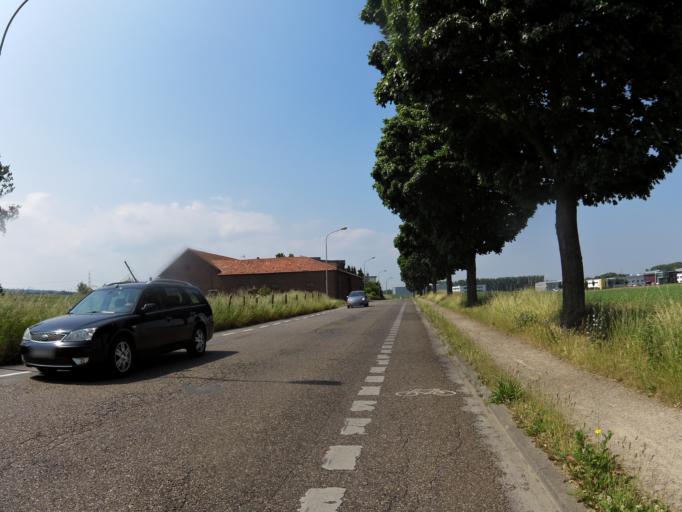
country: DE
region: North Rhine-Westphalia
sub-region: Regierungsbezirk Koln
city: Aachen
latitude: 50.8230
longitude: 6.0870
